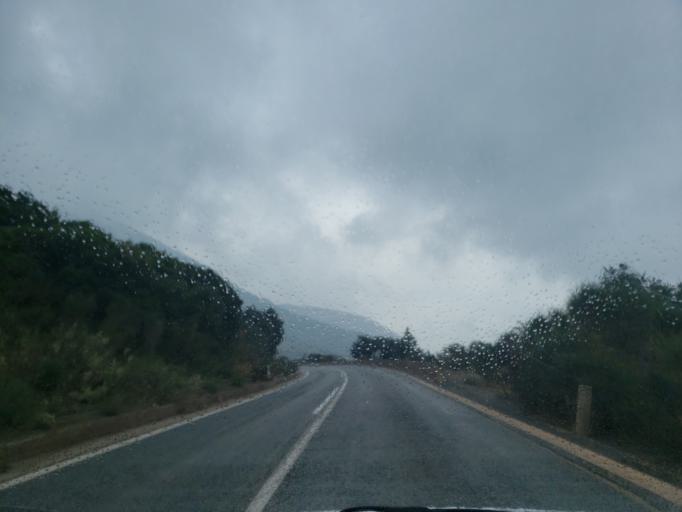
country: GR
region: Central Greece
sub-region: Nomos Fokidos
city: Amfissa
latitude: 38.5903
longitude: 22.3853
